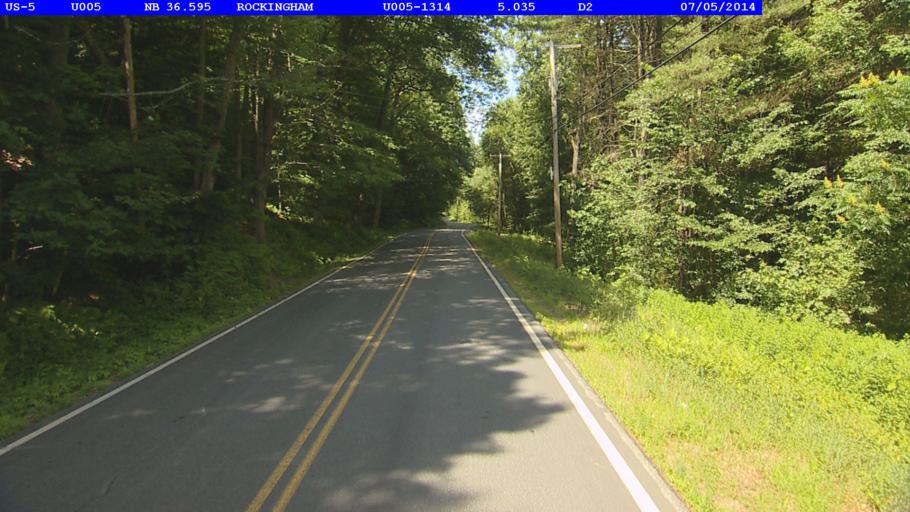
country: US
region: Vermont
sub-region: Windham County
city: Rockingham
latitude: 43.1882
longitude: -72.4503
